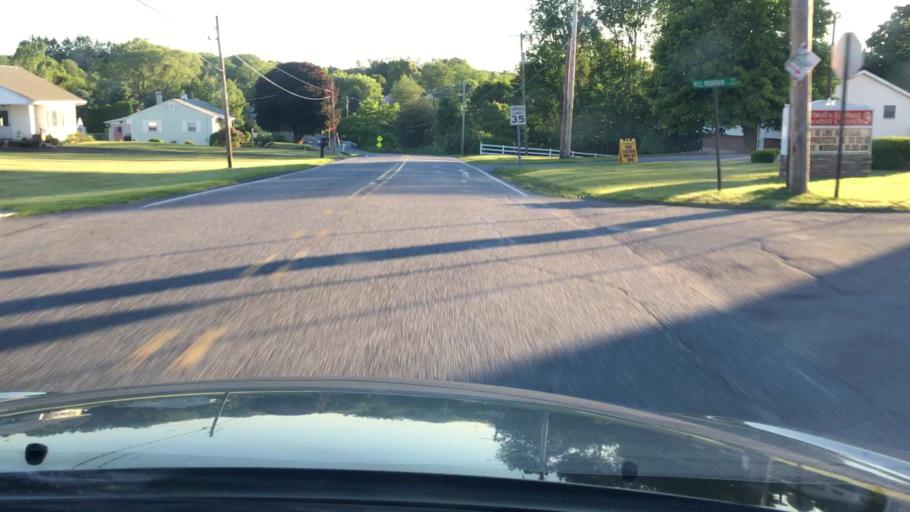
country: US
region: Pennsylvania
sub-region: Luzerne County
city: Harleigh
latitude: 41.0181
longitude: -75.9947
